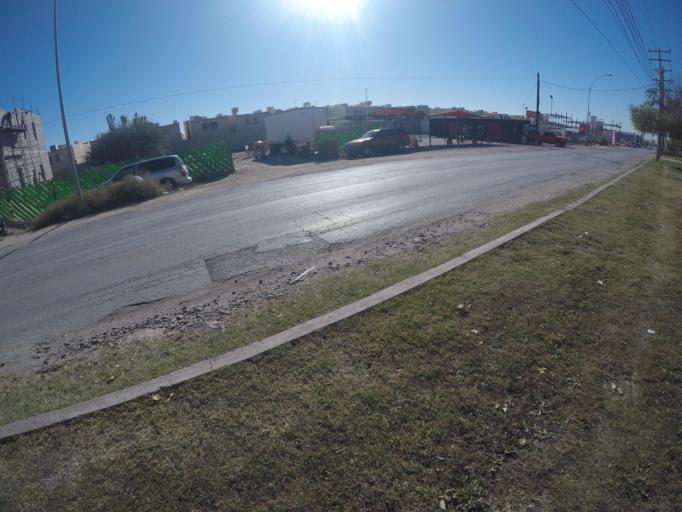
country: US
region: Texas
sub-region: El Paso County
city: Socorro
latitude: 31.6968
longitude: -106.3739
